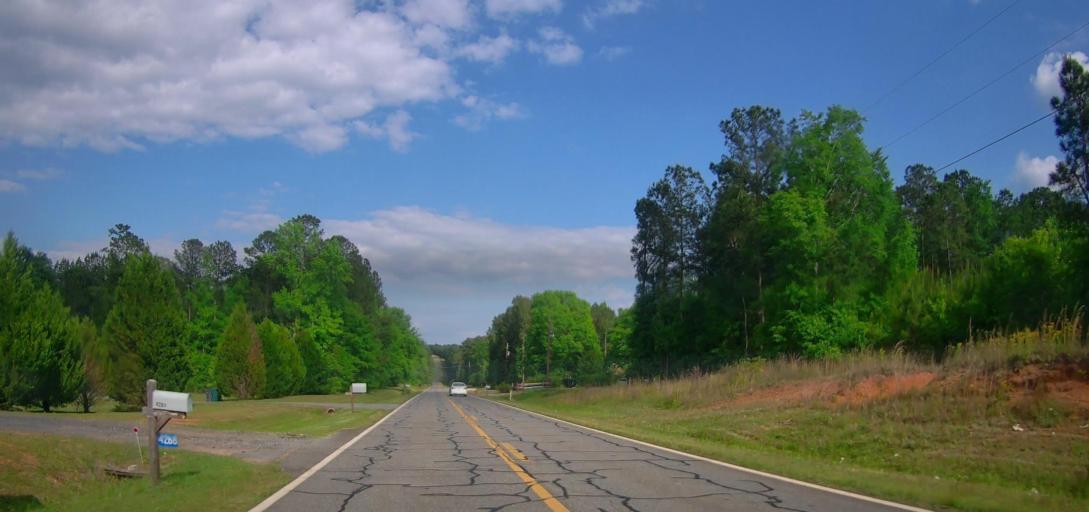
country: US
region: Georgia
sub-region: Baldwin County
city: Hardwick
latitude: 33.0638
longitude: -83.1660
